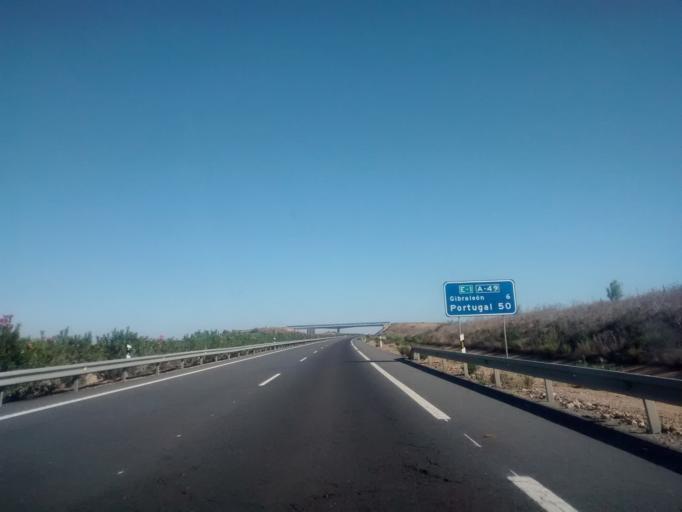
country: ES
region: Andalusia
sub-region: Provincia de Huelva
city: Huelva
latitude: 37.3307
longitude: -6.9151
